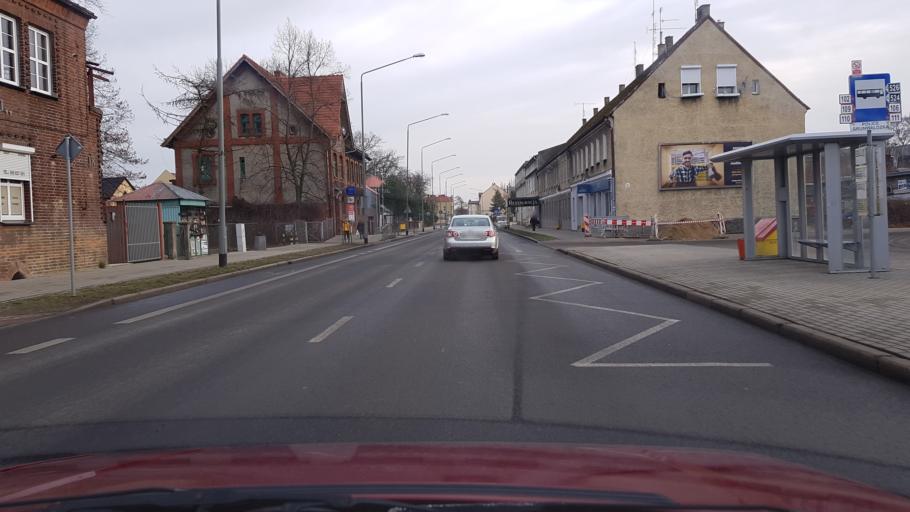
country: PL
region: West Pomeranian Voivodeship
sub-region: Powiat policki
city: Police
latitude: 53.5514
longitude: 14.5674
